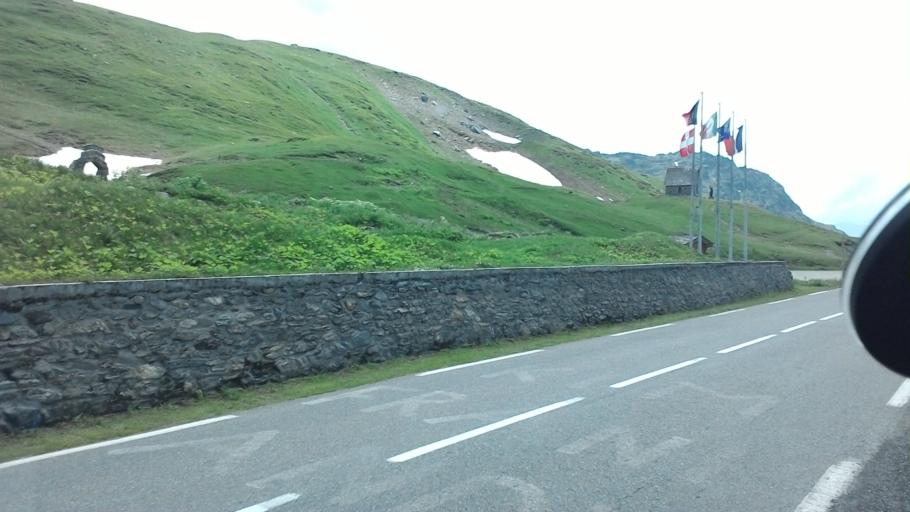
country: IT
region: Aosta Valley
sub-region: Valle d'Aosta
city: La Thuile
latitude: 45.6749
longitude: 6.8795
